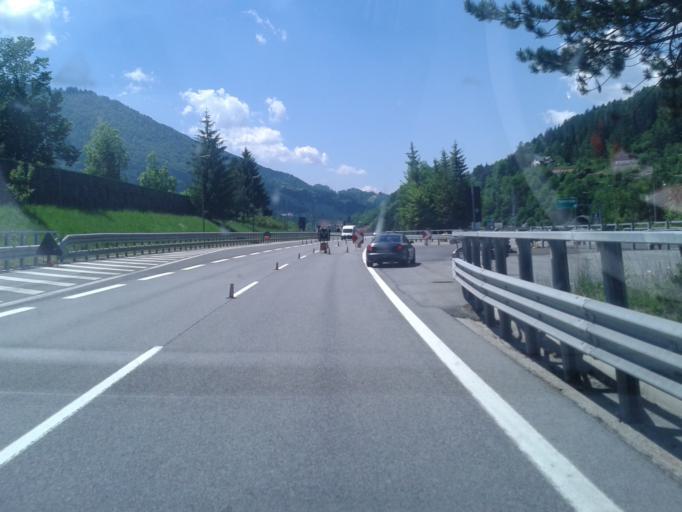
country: IT
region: Friuli Venezia Giulia
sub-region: Provincia di Udine
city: Tarvisio
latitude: 46.5055
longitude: 13.6012
